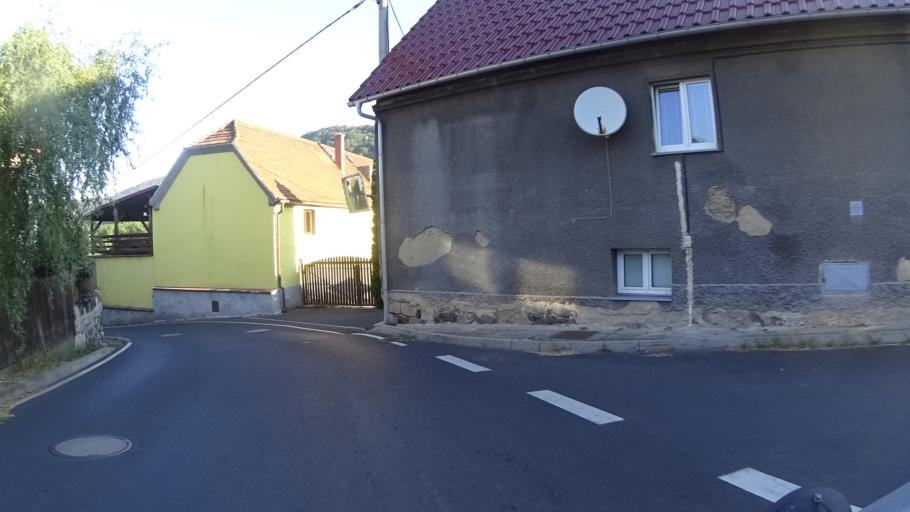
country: CZ
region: Ustecky
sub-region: Okres Usti nad Labem
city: Usti nad Labem
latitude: 50.5939
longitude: 14.0653
